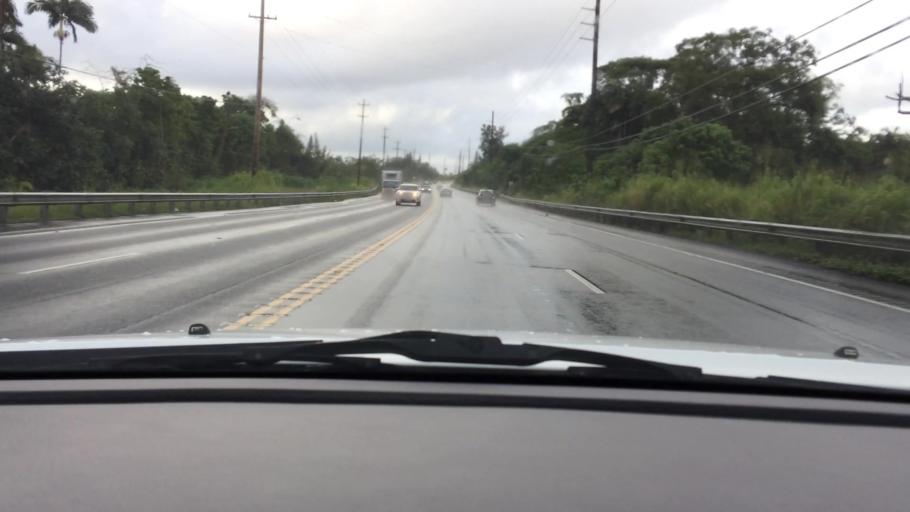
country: US
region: Hawaii
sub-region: Hawaii County
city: Orchidlands Estates
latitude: 19.5885
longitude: -155.0135
